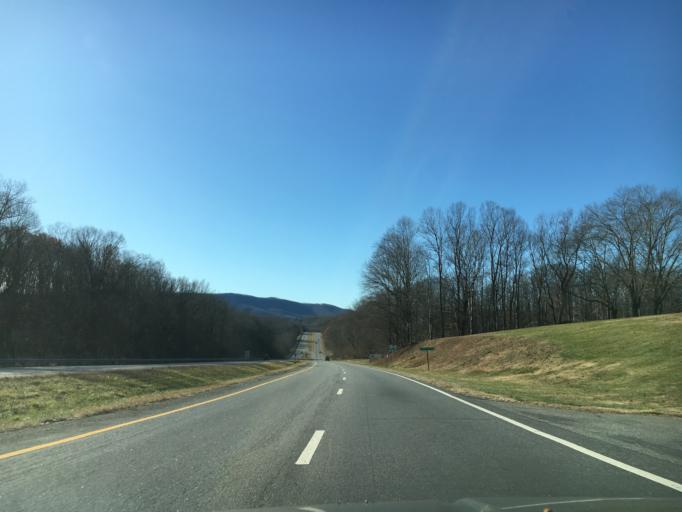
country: US
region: Virginia
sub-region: Patrick County
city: Patrick Springs
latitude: 36.6419
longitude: -80.2281
